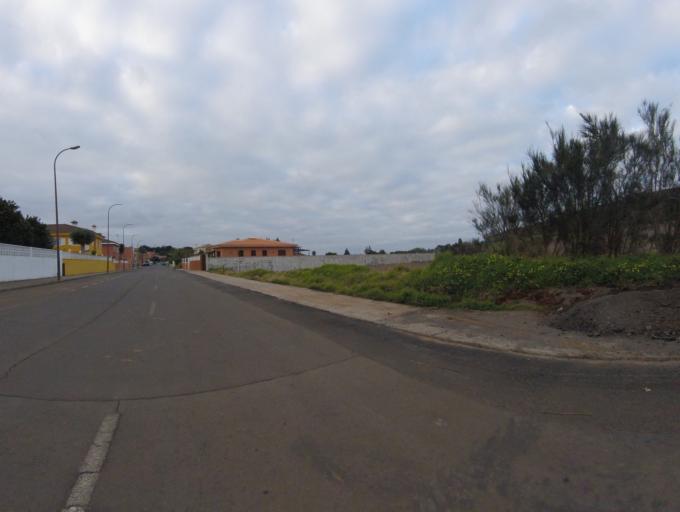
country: ES
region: Canary Islands
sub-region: Provincia de Santa Cruz de Tenerife
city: La Laguna
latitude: 28.4541
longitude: -16.3600
